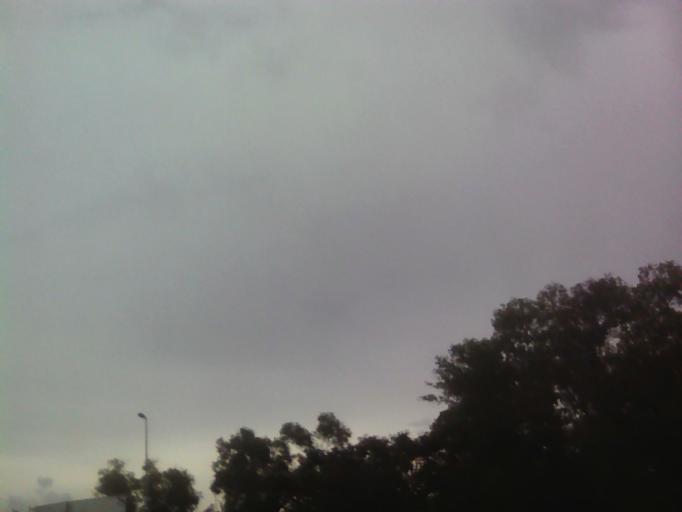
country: MY
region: Penang
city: Perai
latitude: 5.4045
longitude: 100.3940
